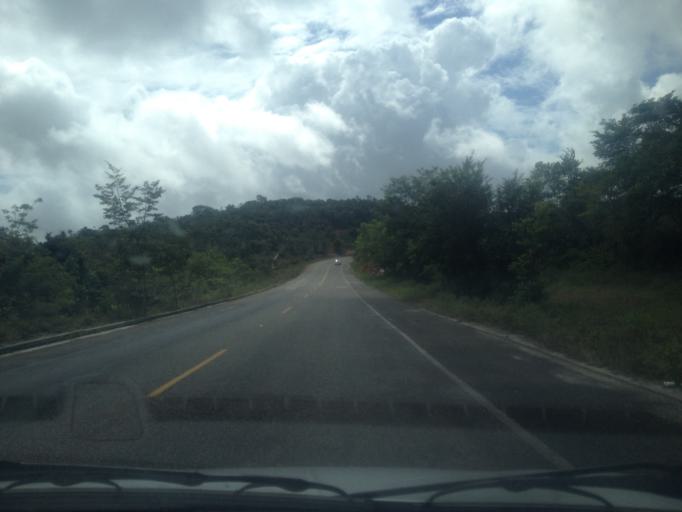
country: BR
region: Bahia
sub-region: Conde
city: Conde
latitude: -12.0875
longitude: -37.7729
